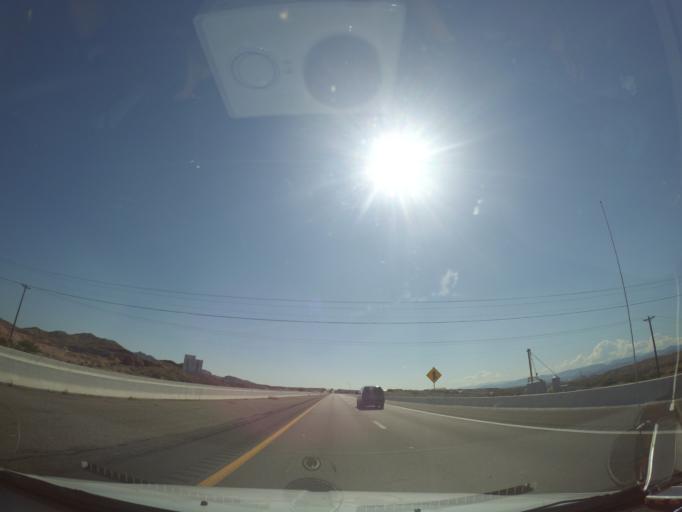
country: US
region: Nevada
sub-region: Clark County
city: Moapa Town
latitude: 36.6606
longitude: -114.5744
